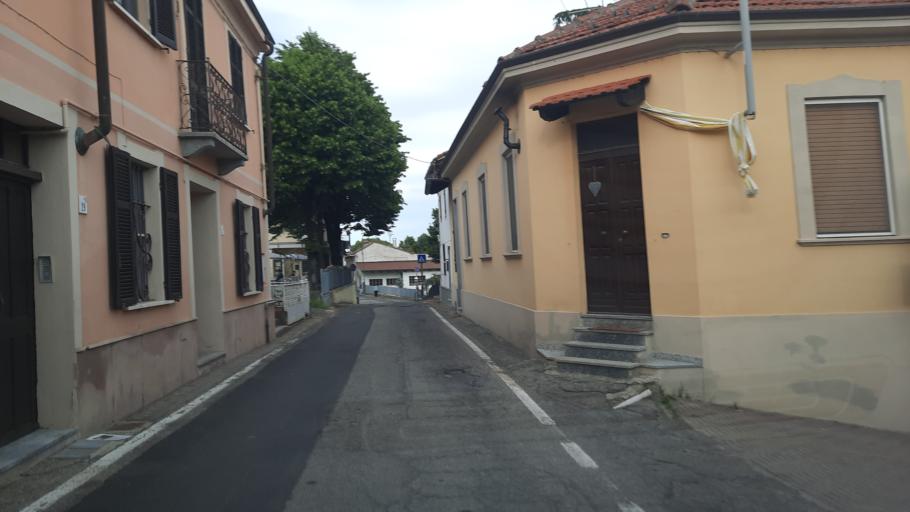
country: IT
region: Piedmont
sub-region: Provincia di Alessandria
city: Coniolo Bricco
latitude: 45.1472
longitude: 8.3715
